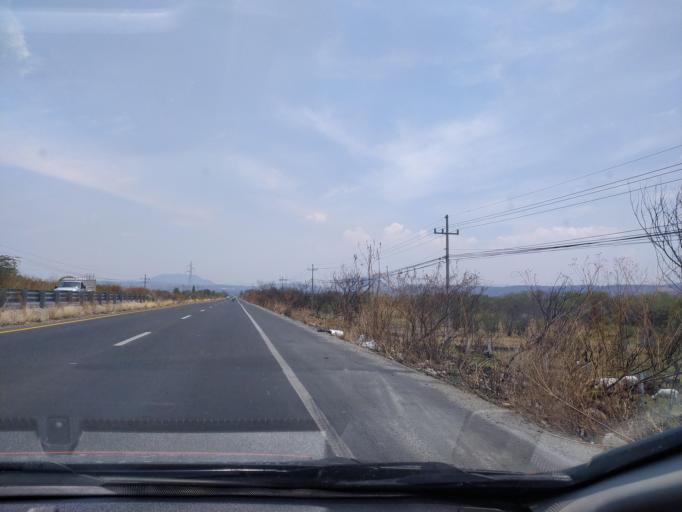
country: MX
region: Jalisco
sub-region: Acatlan de Juarez
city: Villa de los Ninos
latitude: 20.3782
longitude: -103.5927
